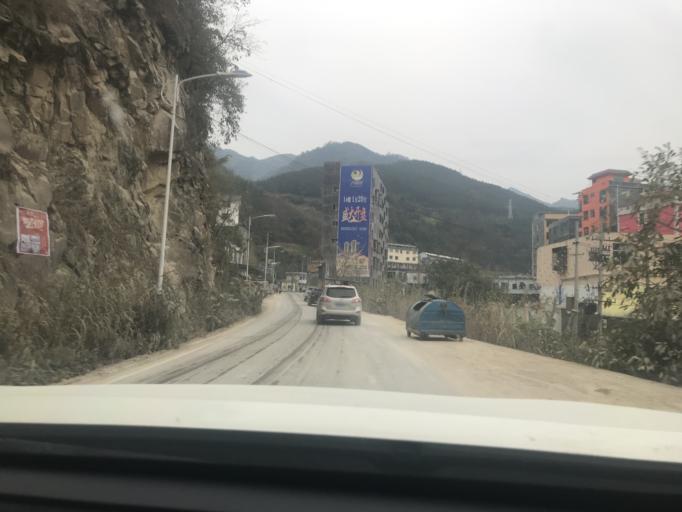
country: CN
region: Guangxi Zhuangzu Zizhiqu
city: Xinzhou
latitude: 24.9835
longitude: 105.8186
